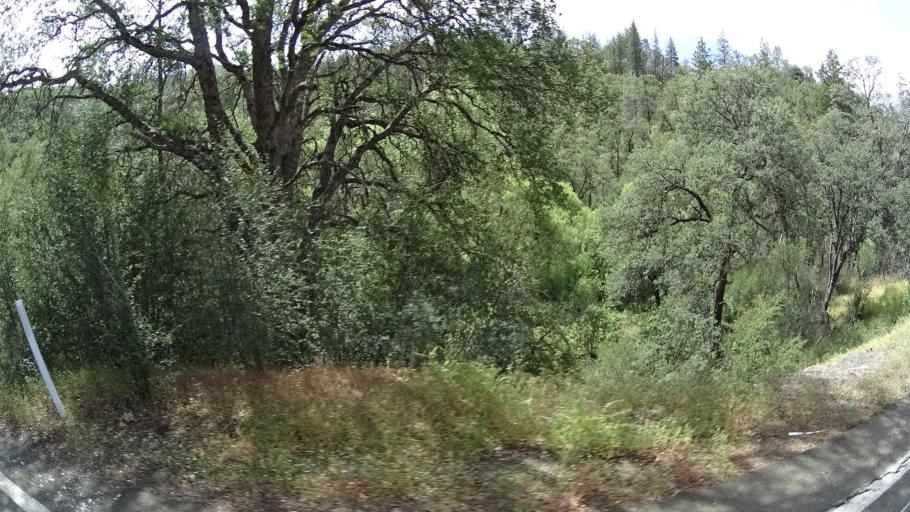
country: US
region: California
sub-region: Lake County
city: Lower Lake
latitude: 38.8835
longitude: -122.6688
